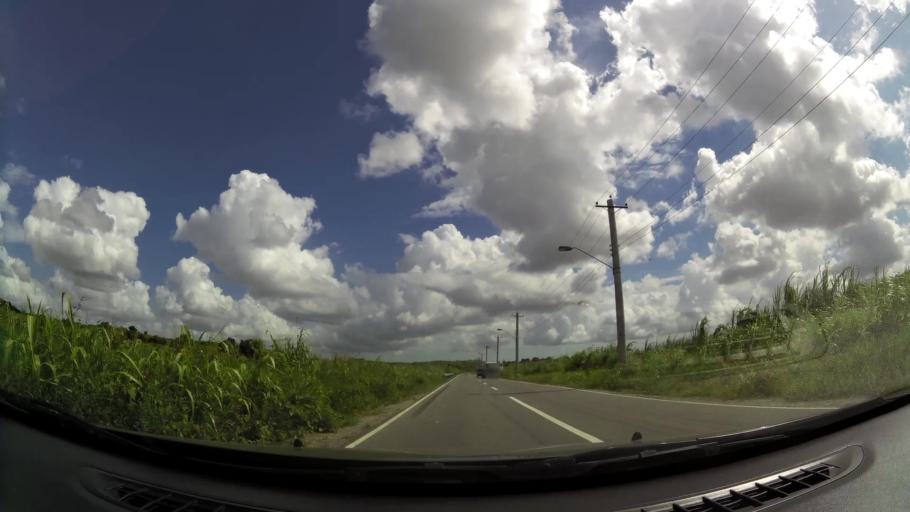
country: TT
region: Penal/Debe
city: Debe
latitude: 10.2344
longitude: -61.4953
